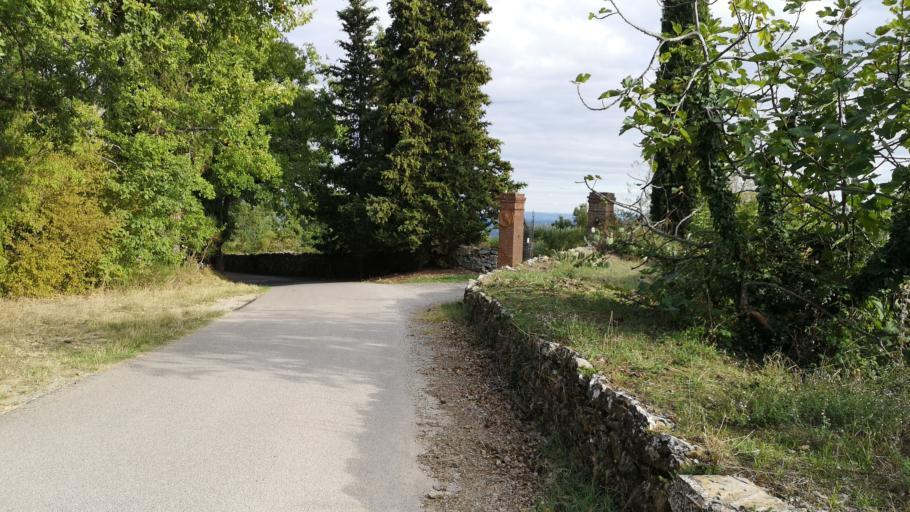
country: IT
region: Tuscany
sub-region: Provincia di Siena
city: Castellina in Chianti
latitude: 43.4319
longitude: 11.3394
